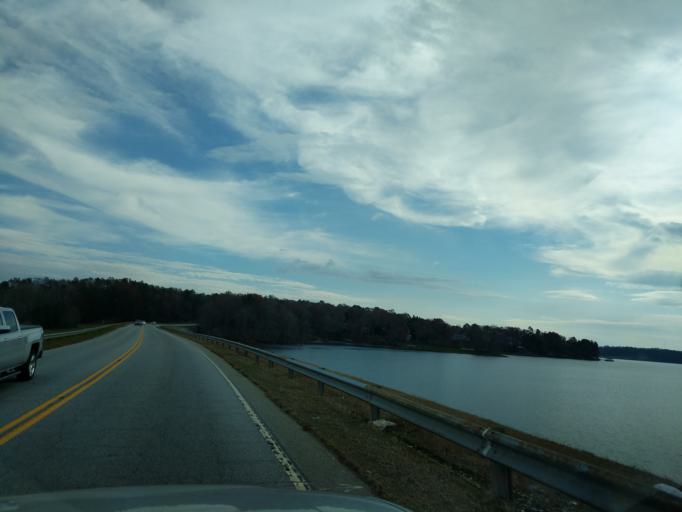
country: US
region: South Carolina
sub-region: Oconee County
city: Utica
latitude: 34.7478
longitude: -82.9087
